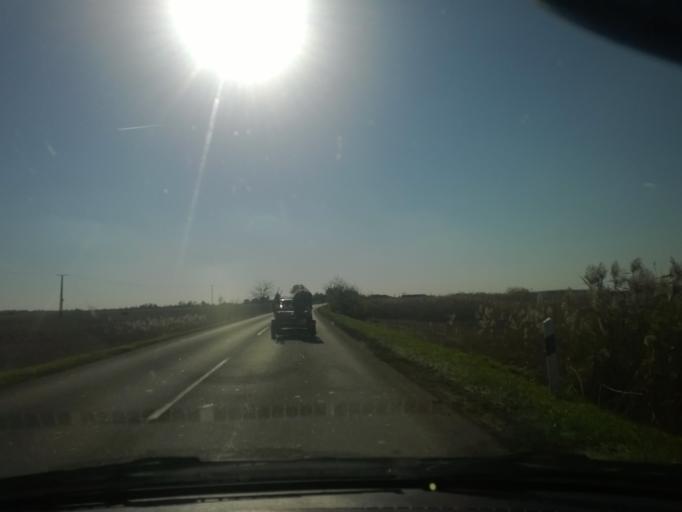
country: HU
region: Csongrad
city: Szegvar
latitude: 46.5454
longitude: 20.3171
